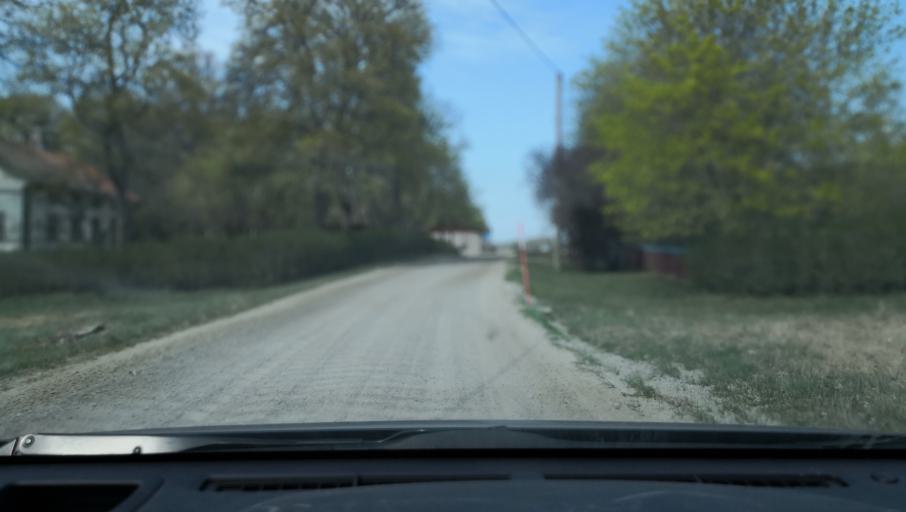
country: SE
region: Vaestmanland
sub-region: Vasteras
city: Skultuna
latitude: 59.7850
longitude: 16.4584
